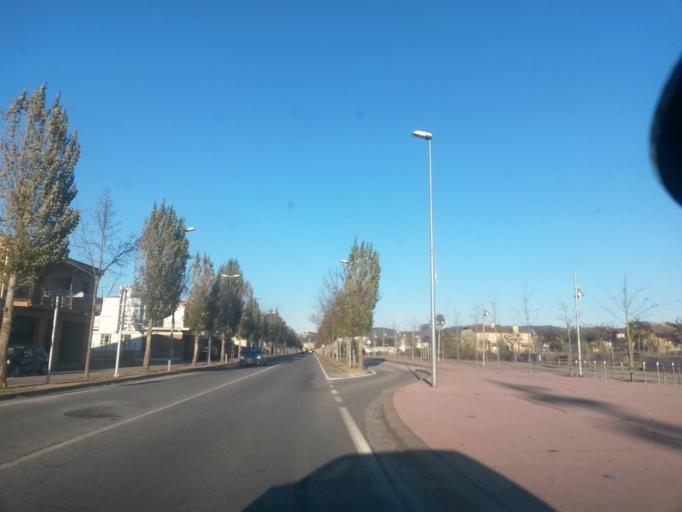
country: ES
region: Catalonia
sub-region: Provincia de Girona
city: Salt
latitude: 41.9529
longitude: 2.7957
